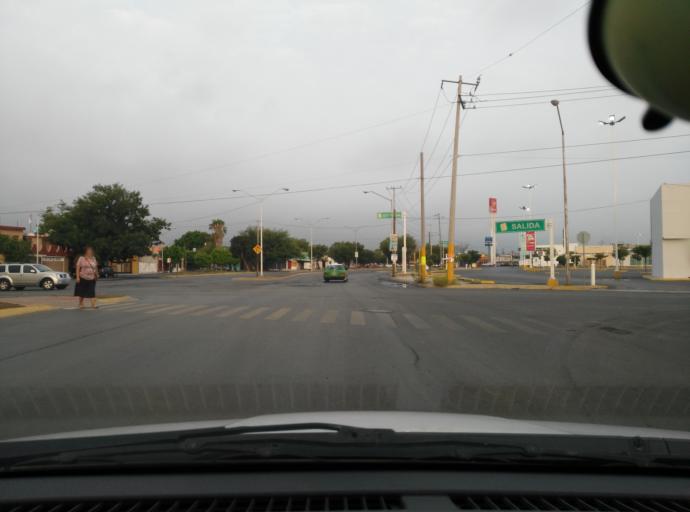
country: MX
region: Nuevo Leon
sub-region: San Nicolas de los Garza
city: San Nicolas de los Garza
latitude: 25.7721
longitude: -100.2580
